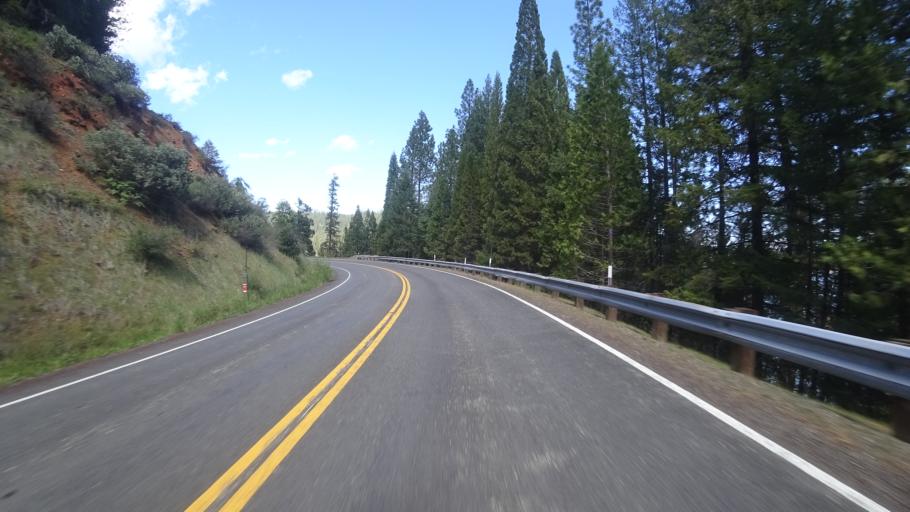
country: US
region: California
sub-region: Trinity County
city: Weaverville
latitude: 40.8403
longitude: -122.8561
